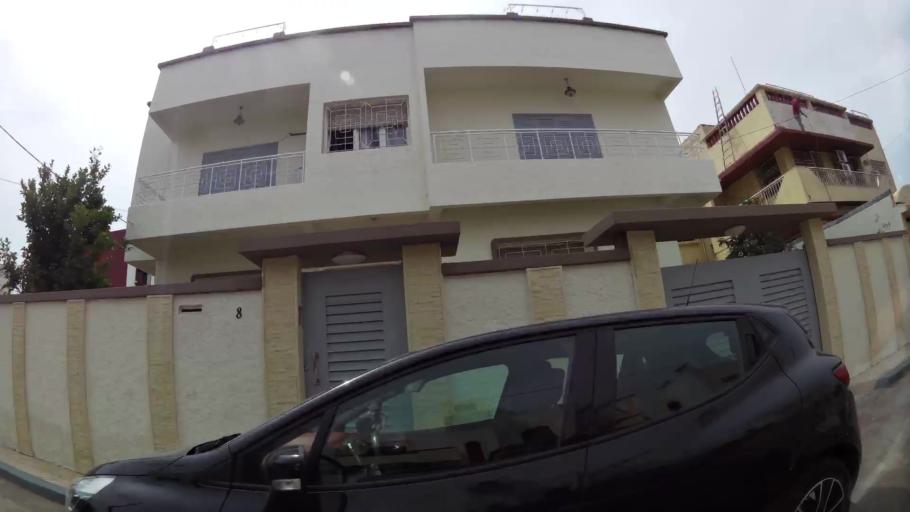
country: MA
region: Rabat-Sale-Zemmour-Zaer
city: Sale
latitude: 34.0268
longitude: -6.8066
